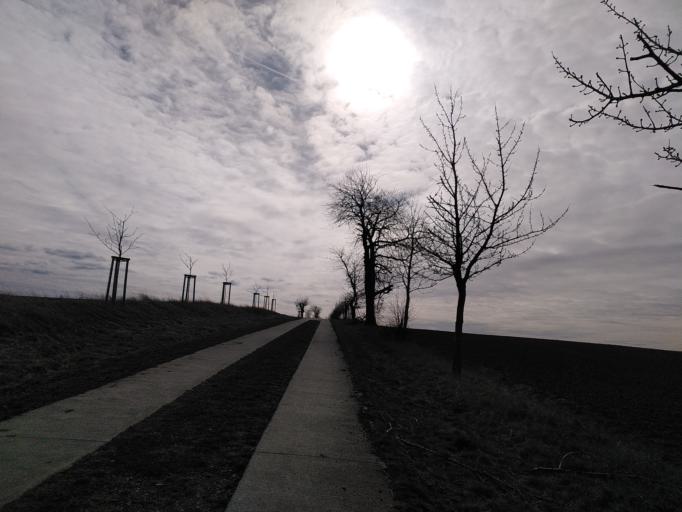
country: DE
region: Saxony-Anhalt
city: Gatersleben
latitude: 51.8129
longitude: 11.2745
